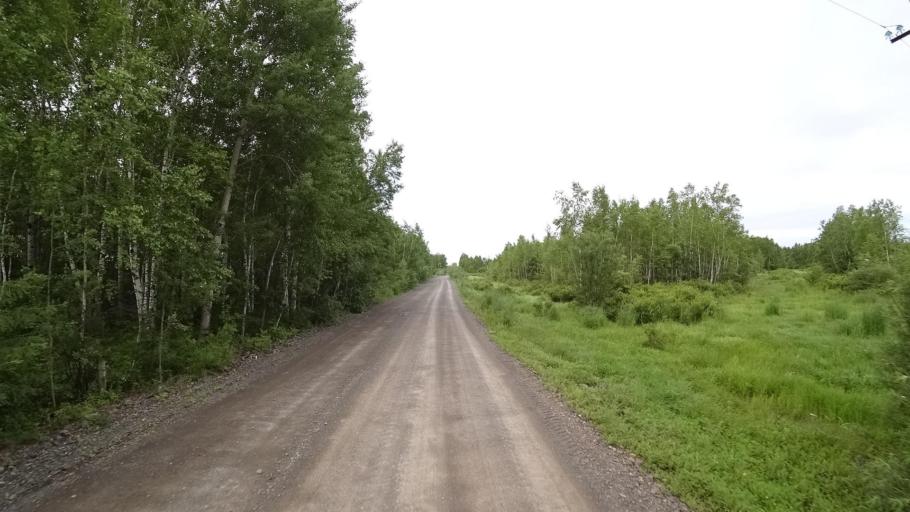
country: RU
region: Khabarovsk Krai
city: Amursk
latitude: 49.9053
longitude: 136.1394
